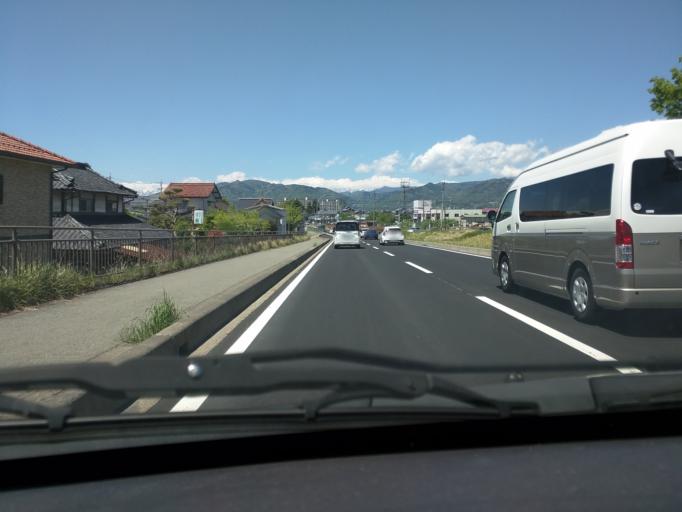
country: JP
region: Nagano
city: Suzaka
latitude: 36.6413
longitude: 138.2527
